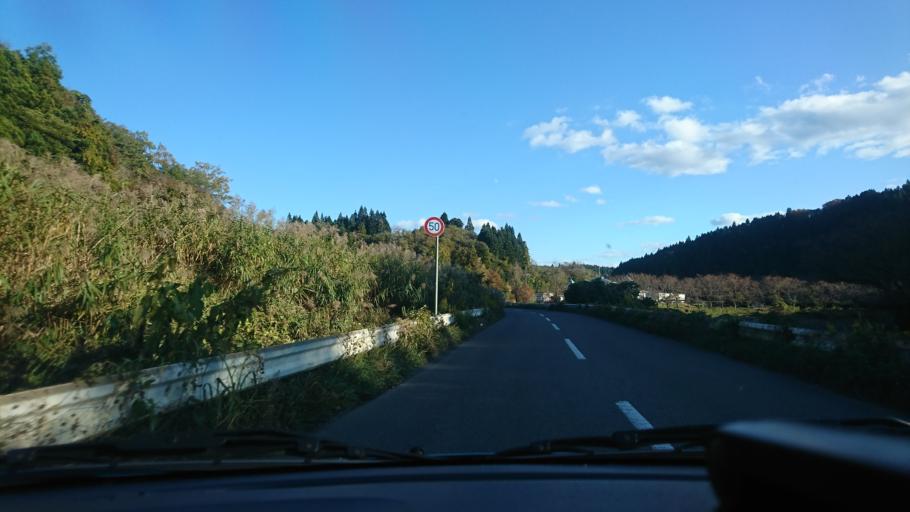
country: JP
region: Iwate
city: Ichinoseki
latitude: 38.8566
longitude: 141.3058
